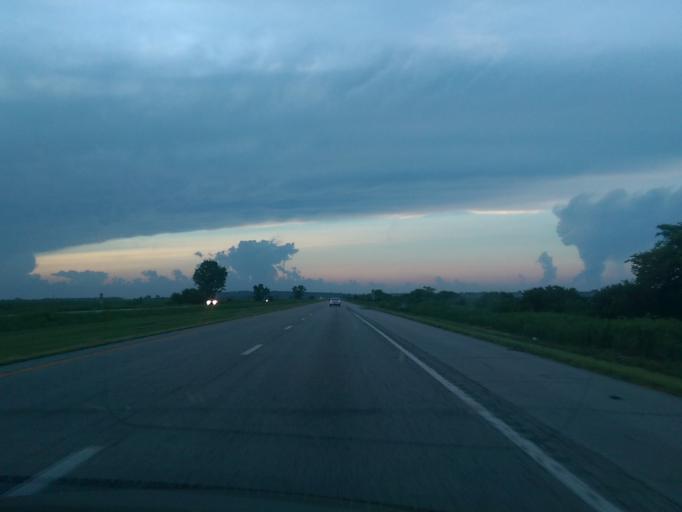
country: US
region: Missouri
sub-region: Atchison County
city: Rock Port
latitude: 40.4990
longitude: -95.5987
